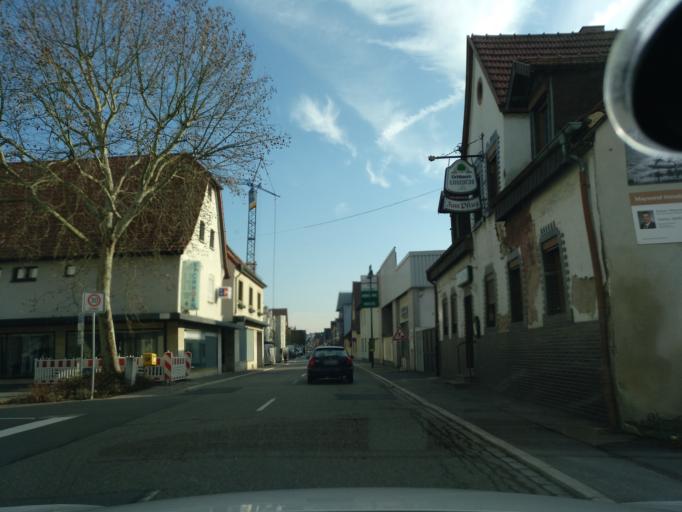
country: DE
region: Baden-Wuerttemberg
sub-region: Karlsruhe Region
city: Hockenheim
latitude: 49.3166
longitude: 8.5490
